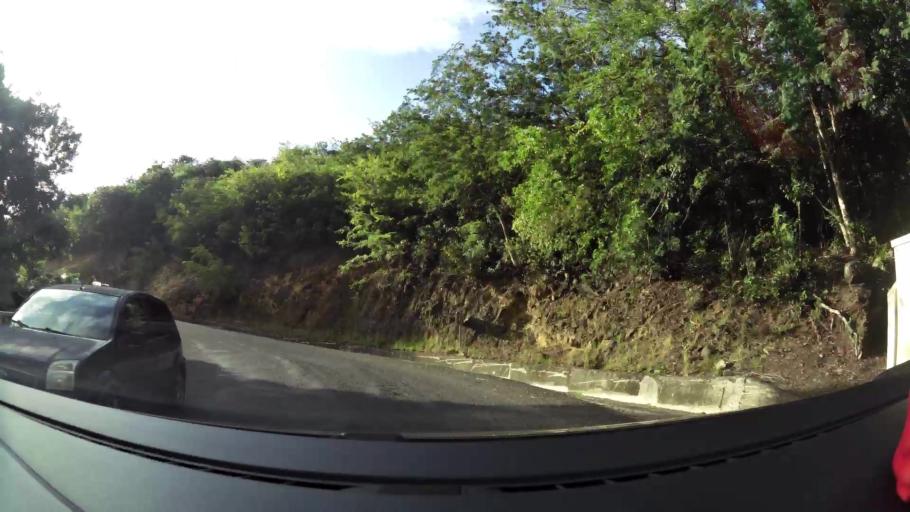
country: GP
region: Guadeloupe
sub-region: Guadeloupe
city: Bouillante
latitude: 16.1777
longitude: -61.7783
